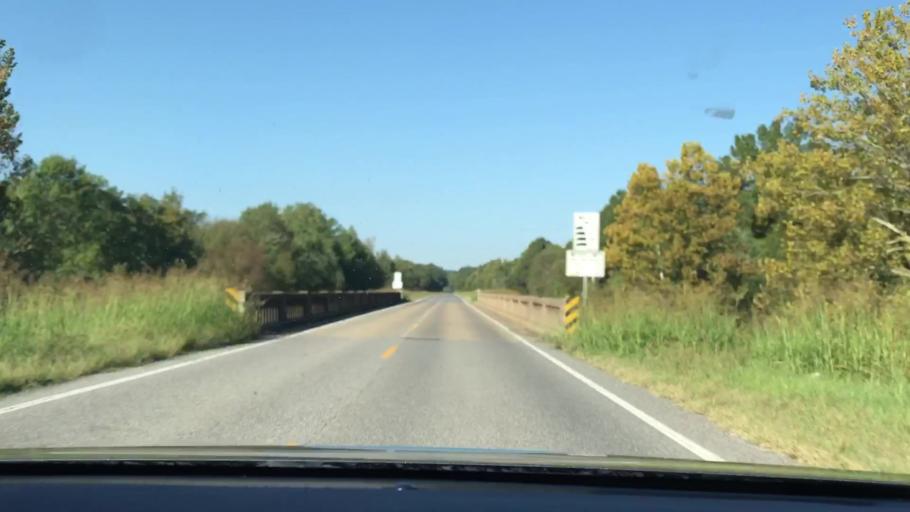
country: US
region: Kentucky
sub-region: Marshall County
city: Benton
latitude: 36.7647
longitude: -88.2320
